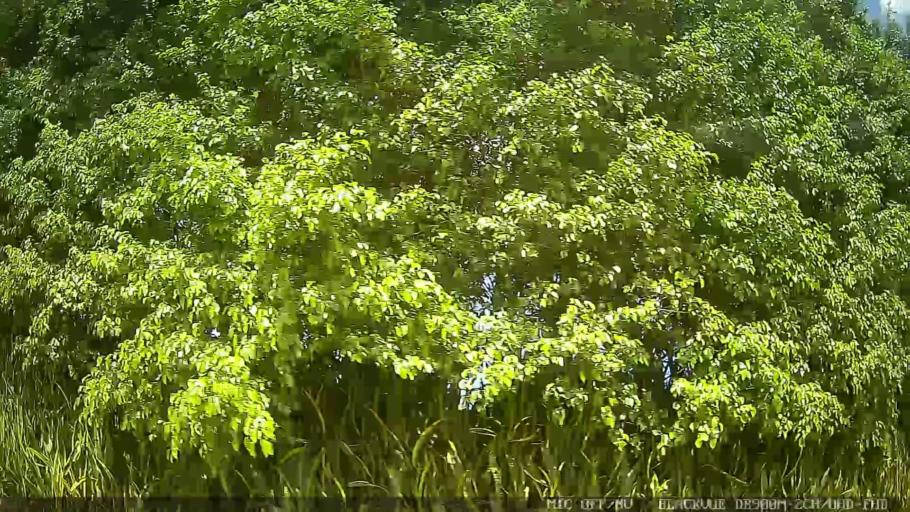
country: BR
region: Sao Paulo
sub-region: Artur Nogueira
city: Artur Nogueira
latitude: -22.6009
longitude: -47.0722
